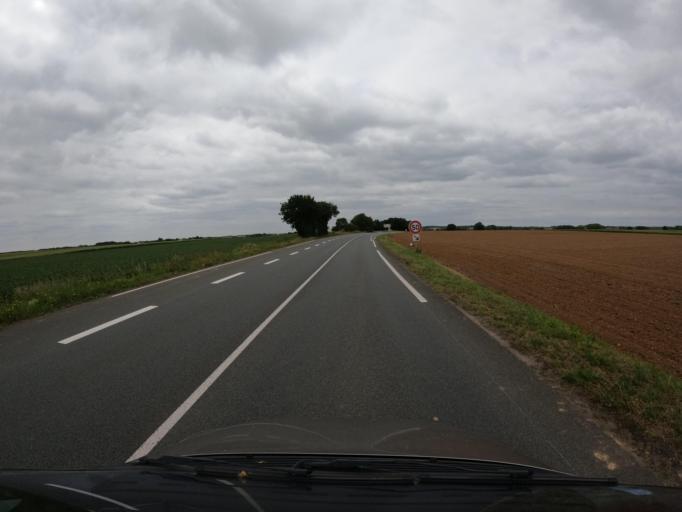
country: FR
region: Pays de la Loire
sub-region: Departement de la Vendee
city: Sainte-Hermine
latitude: 46.5475
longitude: -1.0371
